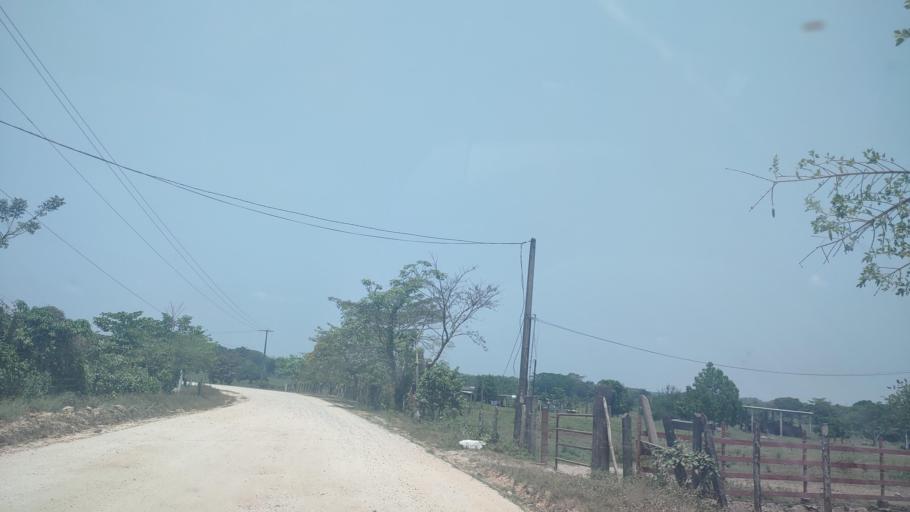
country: MX
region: Tabasco
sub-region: Huimanguillo
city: Francisco Rueda
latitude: 17.6924
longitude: -94.0442
